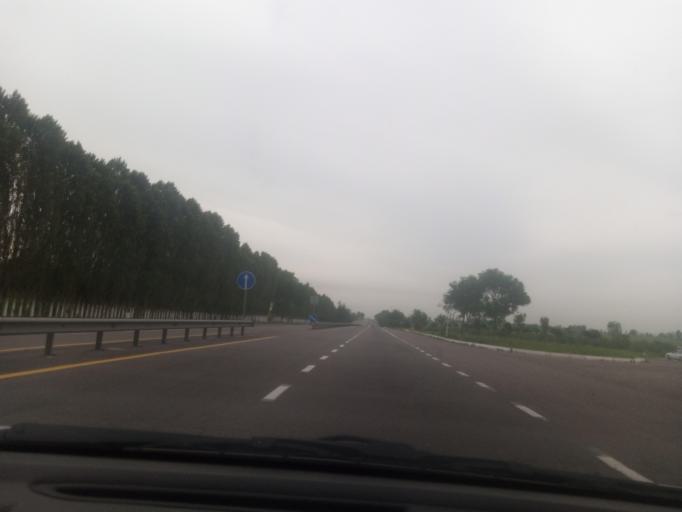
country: UZ
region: Toshkent
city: Tuytepa
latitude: 41.0917
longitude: 69.4621
